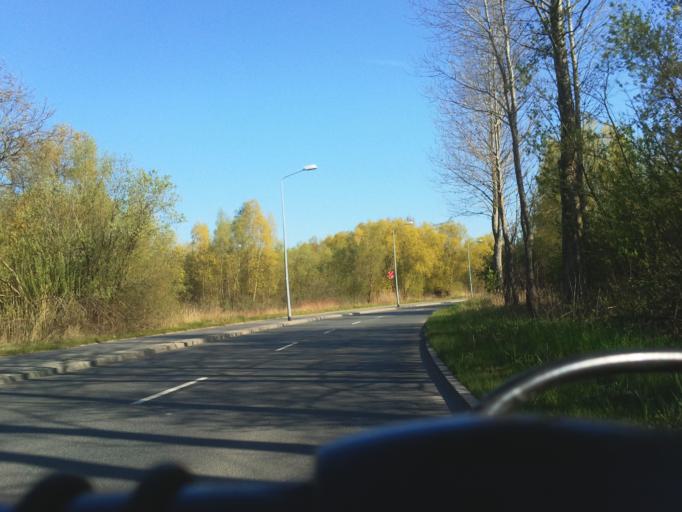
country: DE
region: Mecklenburg-Vorpommern
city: Warnemuende
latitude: 54.1167
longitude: 12.0762
